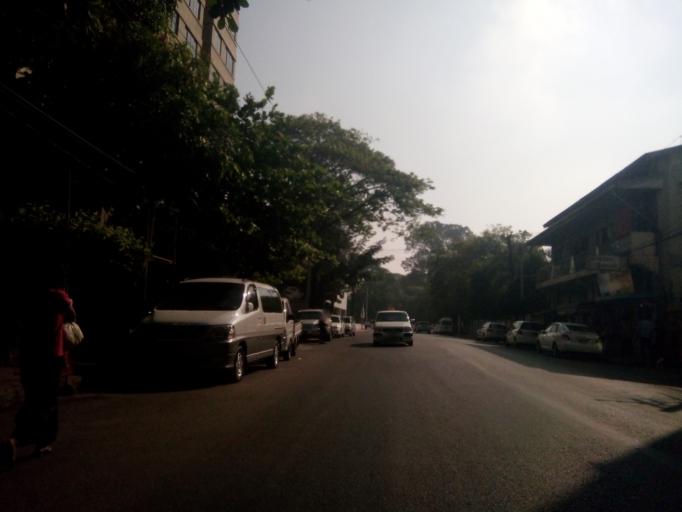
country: MM
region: Yangon
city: Yangon
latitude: 16.8213
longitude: 96.1307
